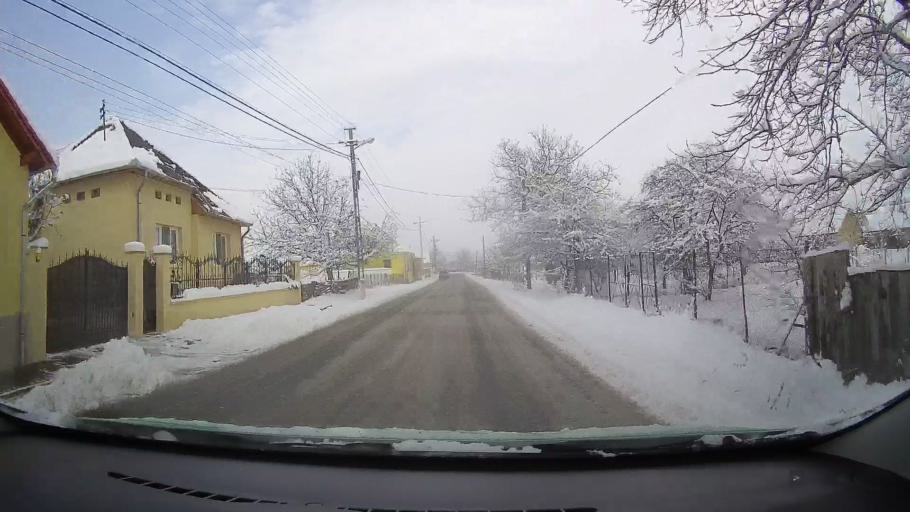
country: RO
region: Alba
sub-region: Comuna Pianu
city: Pianu de Jos
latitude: 45.9397
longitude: 23.4844
